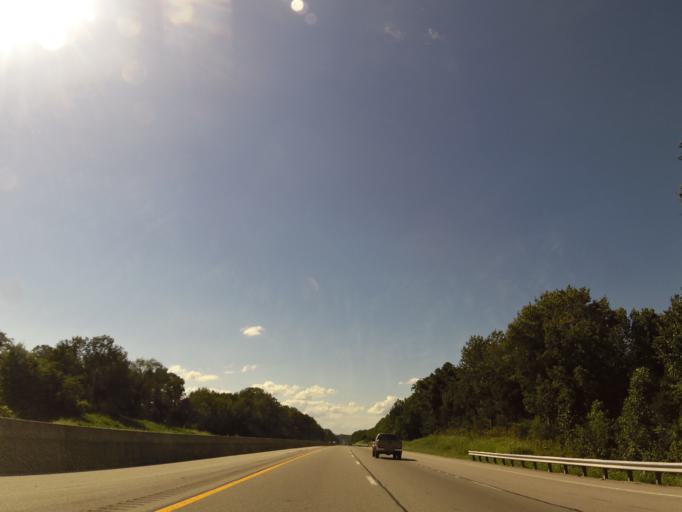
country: US
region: Tennessee
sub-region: Putnam County
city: Lafayette
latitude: 36.0909
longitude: -85.7279
